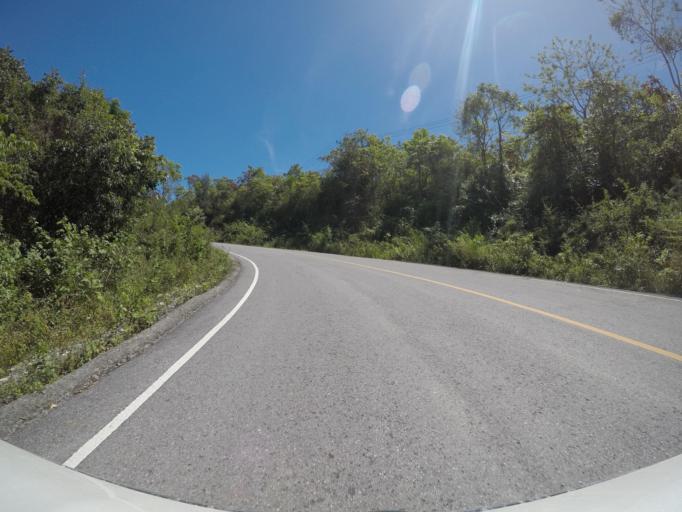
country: TL
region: Manatuto
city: Manatuto
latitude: -8.8142
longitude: 125.9736
